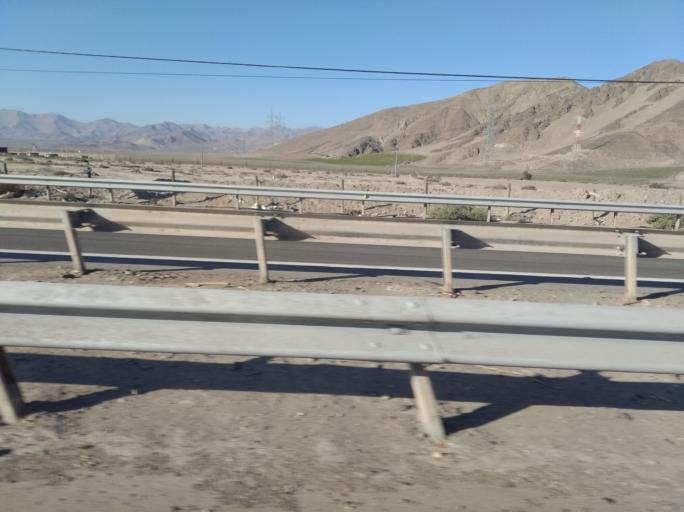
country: CL
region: Atacama
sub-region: Provincia de Copiapo
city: Copiapo
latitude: -27.3195
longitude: -70.4009
